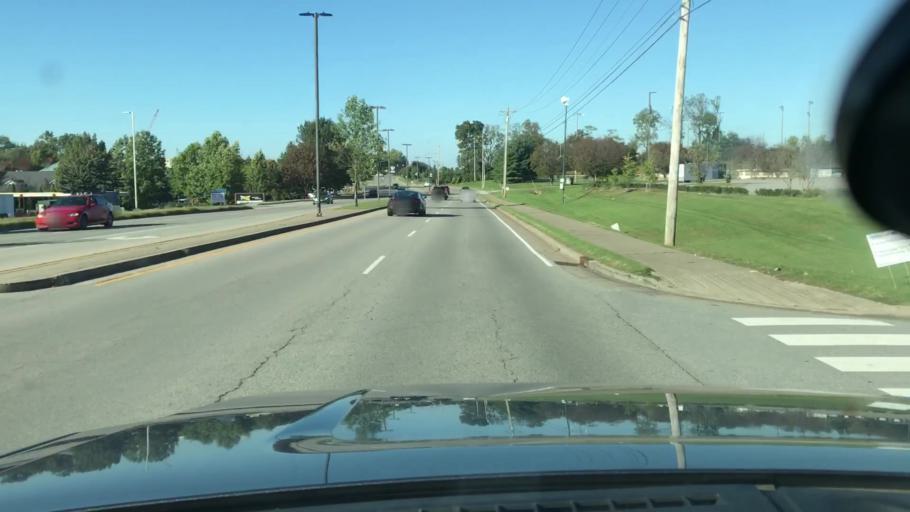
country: US
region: Tennessee
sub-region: Williamson County
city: Franklin
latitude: 35.9307
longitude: -86.8240
